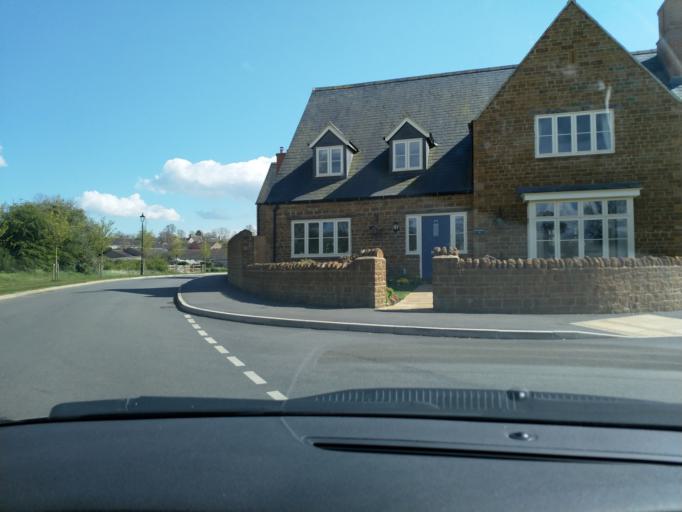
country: GB
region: England
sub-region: Oxfordshire
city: Adderbury
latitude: 52.0264
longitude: -1.2759
